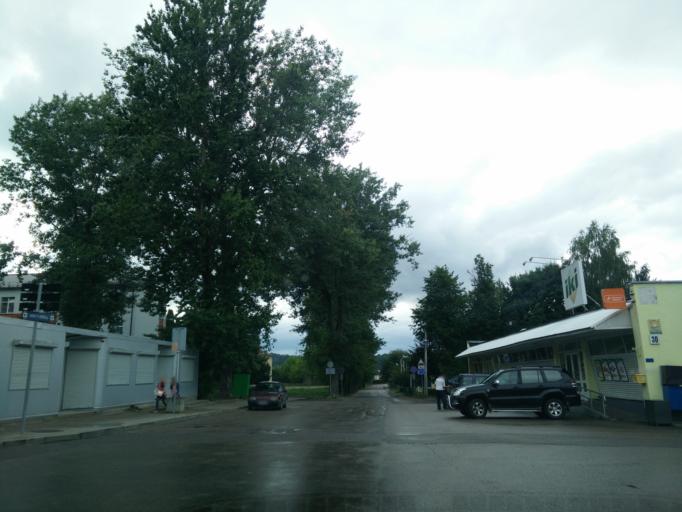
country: LT
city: Grigiskes
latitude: 54.6710
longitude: 25.0912
